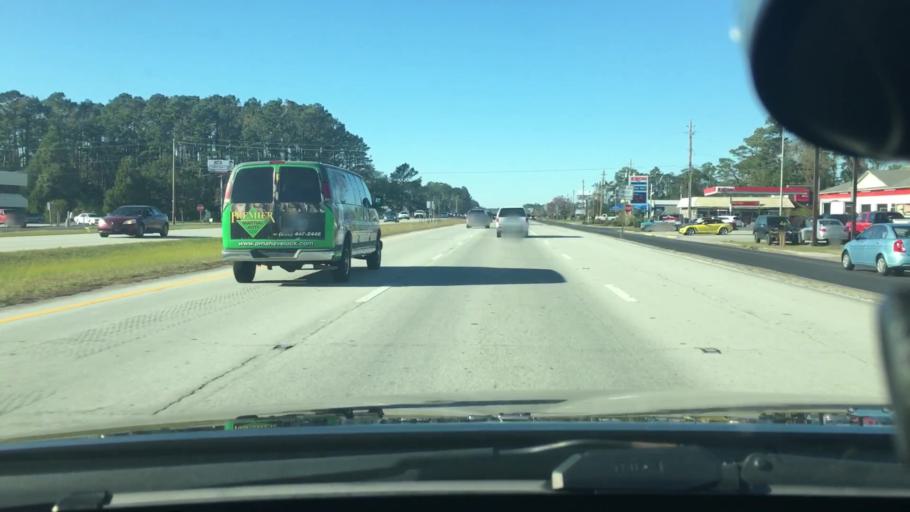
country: US
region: North Carolina
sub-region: Craven County
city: Havelock
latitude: 34.8987
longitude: -76.9289
